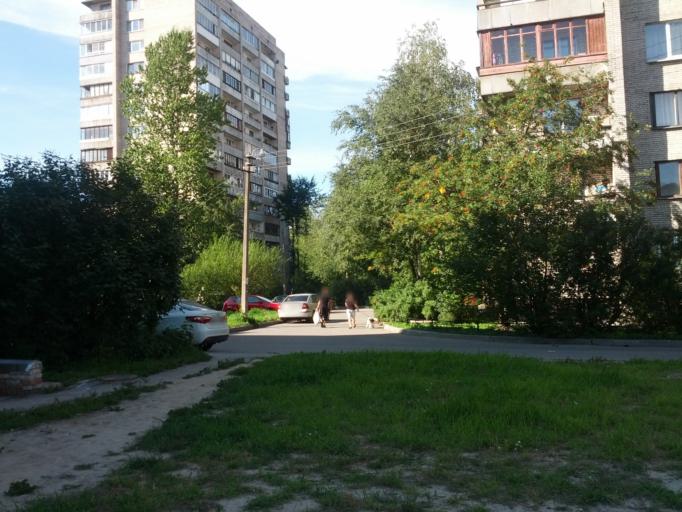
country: RU
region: Leningrad
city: Rybatskoye
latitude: 59.8947
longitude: 30.4874
